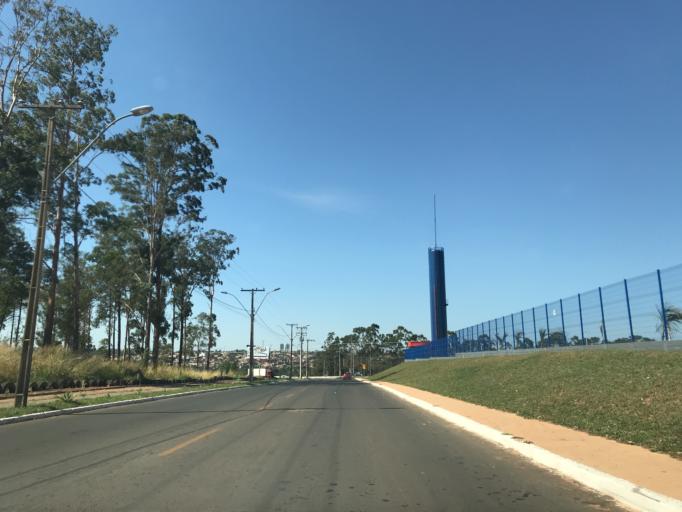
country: BR
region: Federal District
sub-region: Brasilia
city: Brasilia
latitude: -15.8331
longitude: -48.0727
